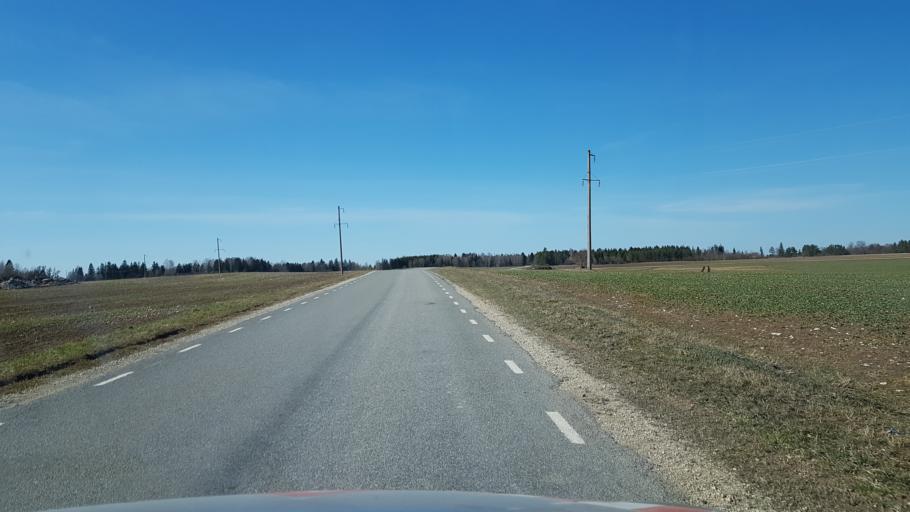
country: EE
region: Laeaene-Virumaa
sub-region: Someru vald
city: Someru
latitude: 59.3528
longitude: 26.4818
